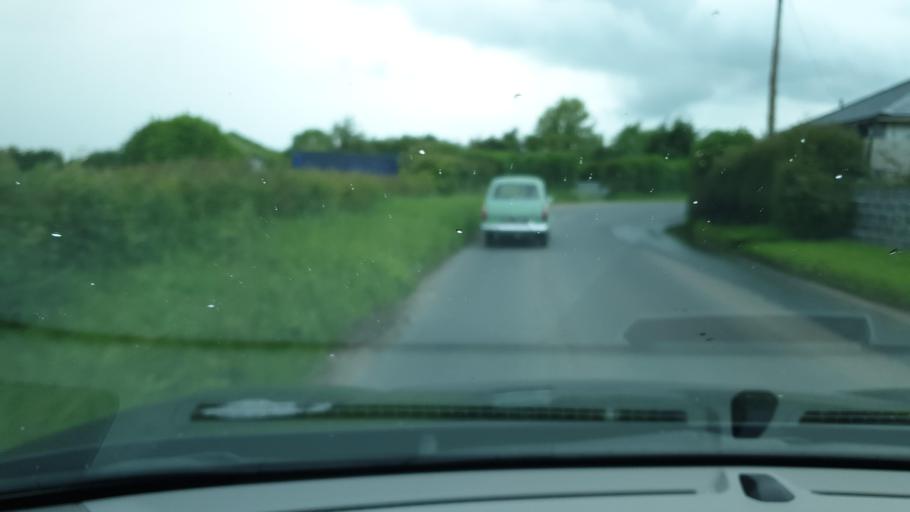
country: IE
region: Leinster
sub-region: An Mhi
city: Ashbourne
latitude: 53.5420
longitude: -6.4111
